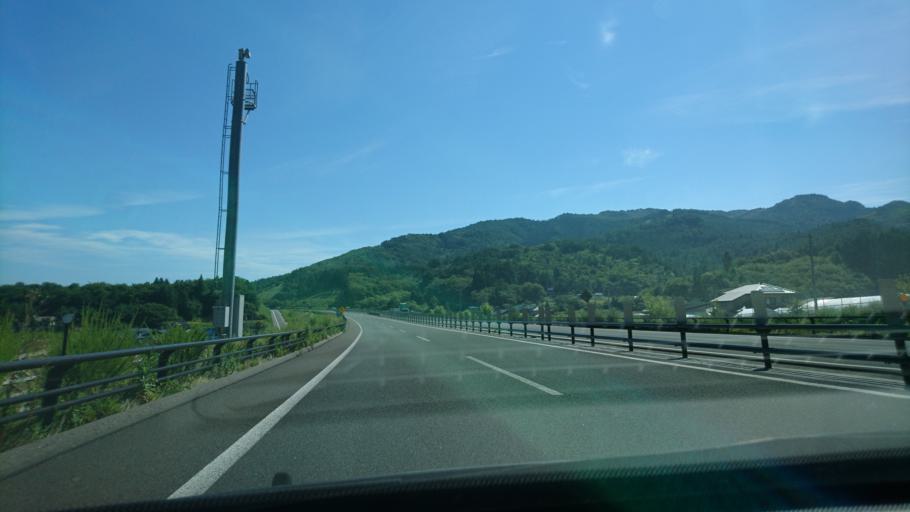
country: JP
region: Iwate
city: Tono
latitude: 39.2935
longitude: 141.4015
